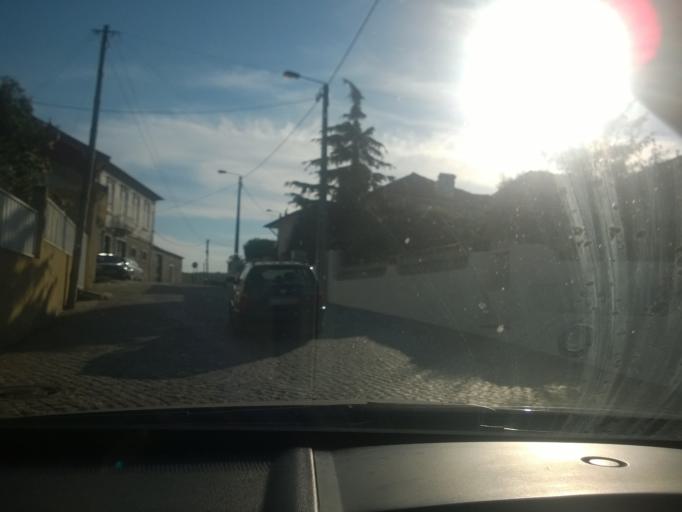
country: PT
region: Porto
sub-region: Maia
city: Anta
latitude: 41.2771
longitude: -8.6151
